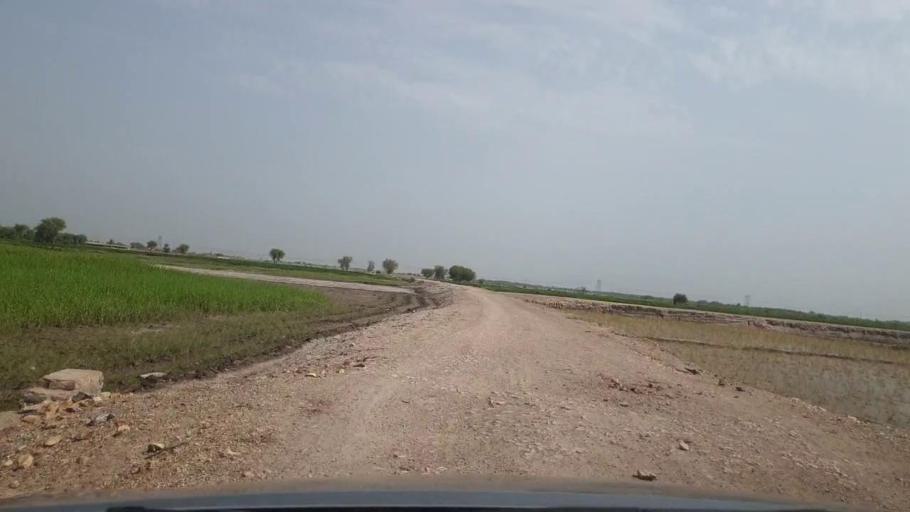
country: PK
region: Sindh
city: Rohri
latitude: 27.6623
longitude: 69.0259
